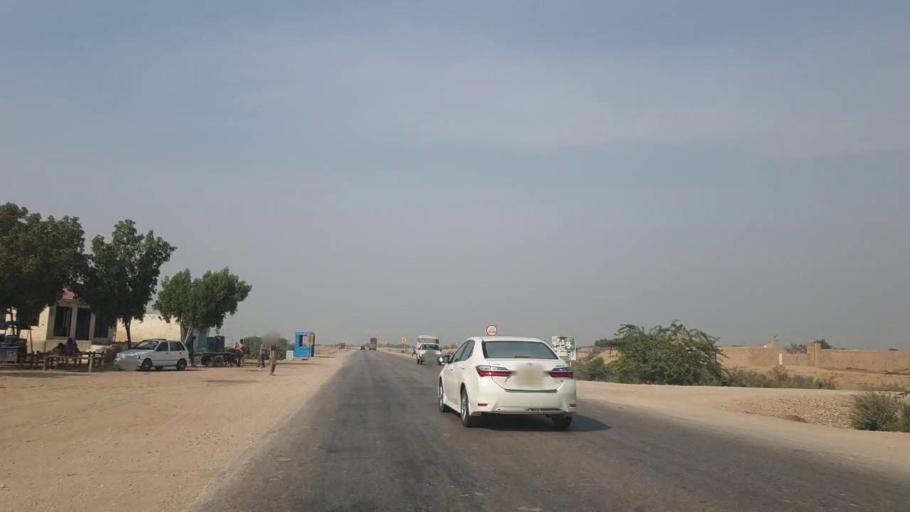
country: PK
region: Sindh
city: Sann
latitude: 26.0884
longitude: 68.0910
